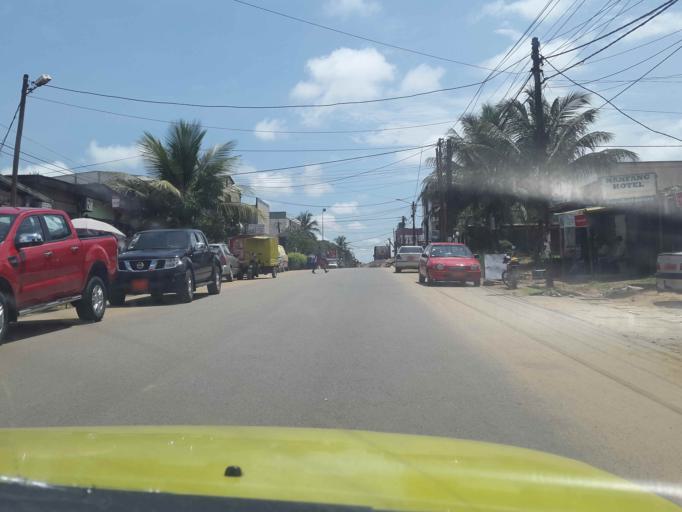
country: CM
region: Littoral
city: Douala
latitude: 4.0909
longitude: 9.7466
